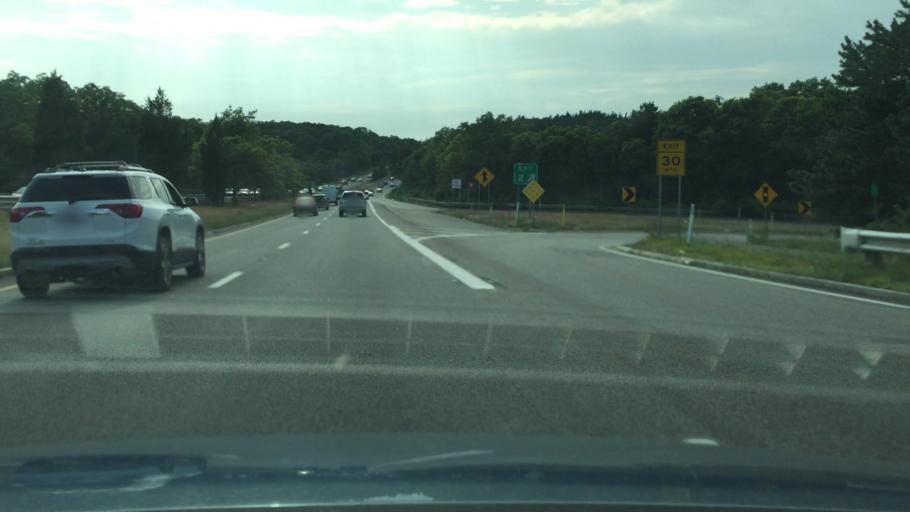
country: US
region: Massachusetts
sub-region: Barnstable County
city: Sandwich
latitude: 41.7393
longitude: -70.4933
